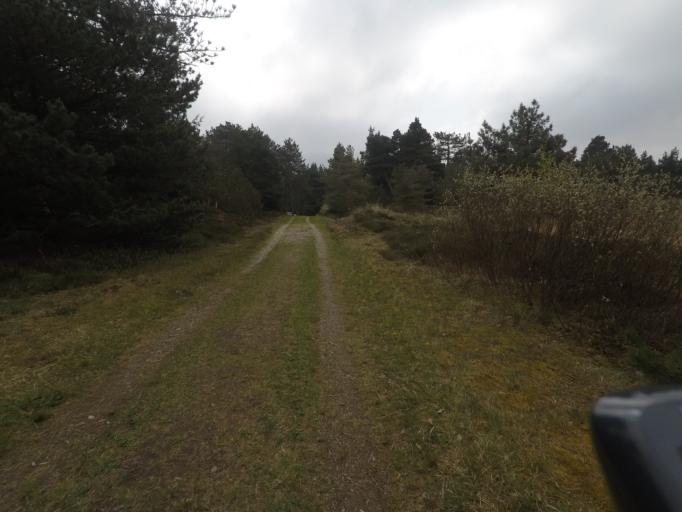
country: DE
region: Schleswig-Holstein
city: List
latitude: 55.1024
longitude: 8.5241
